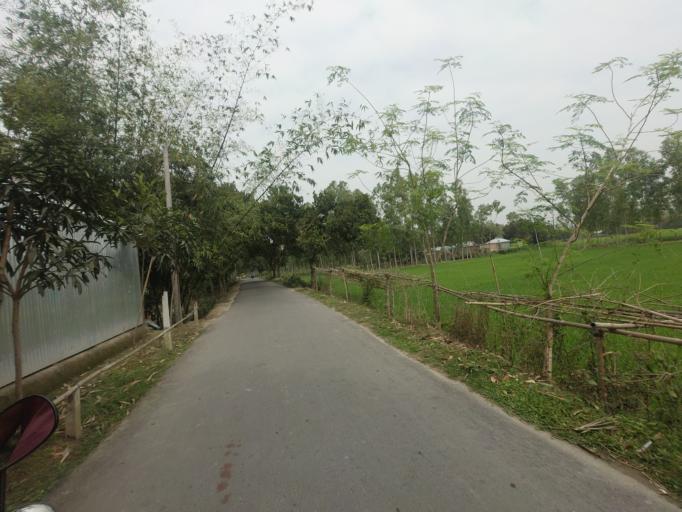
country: BD
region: Rajshahi
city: Sirajganj
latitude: 24.3536
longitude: 89.6711
